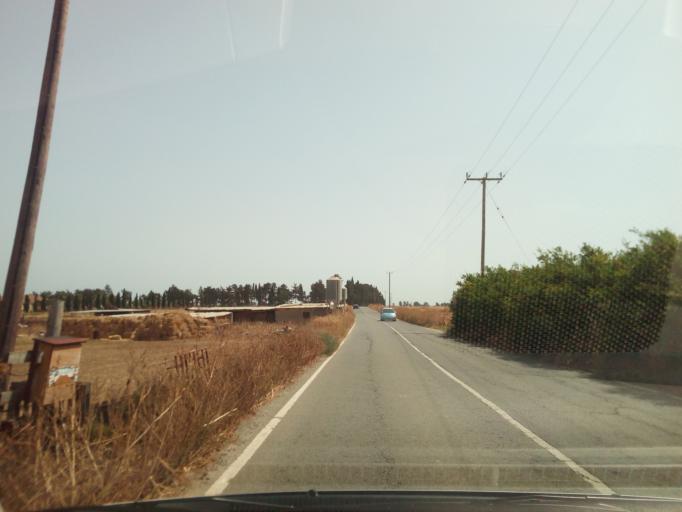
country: CY
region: Larnaka
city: Meneou
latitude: 34.8492
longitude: 33.5946
